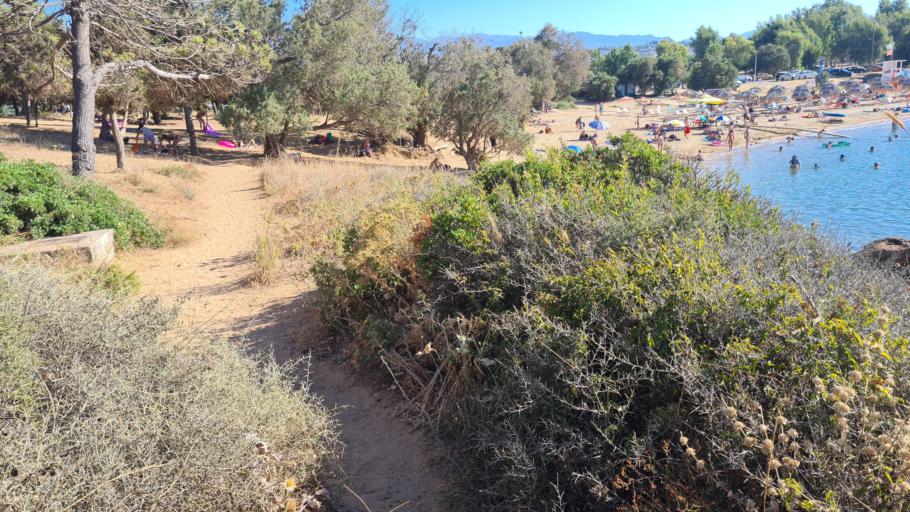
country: GR
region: Crete
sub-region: Nomos Chanias
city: Daratsos
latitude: 35.5147
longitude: 23.9843
